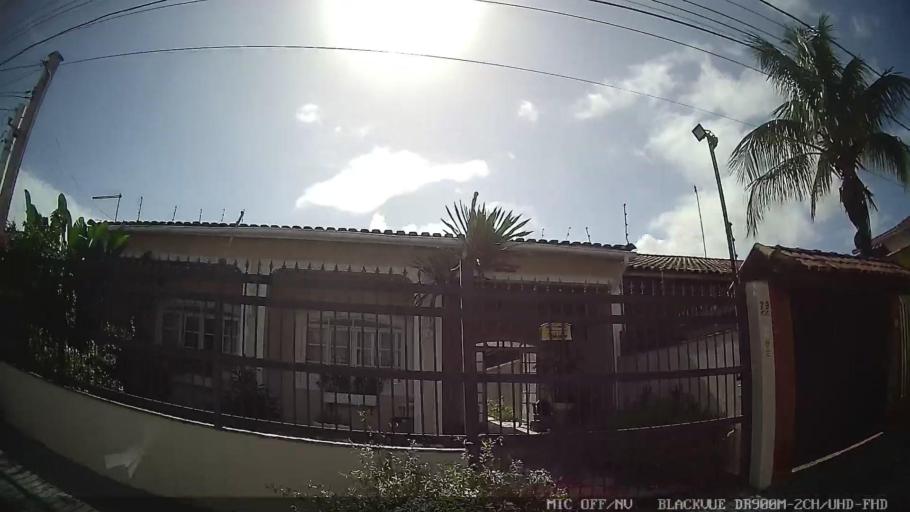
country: BR
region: Sao Paulo
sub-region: Itanhaem
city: Itanhaem
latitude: -24.1609
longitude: -46.7439
